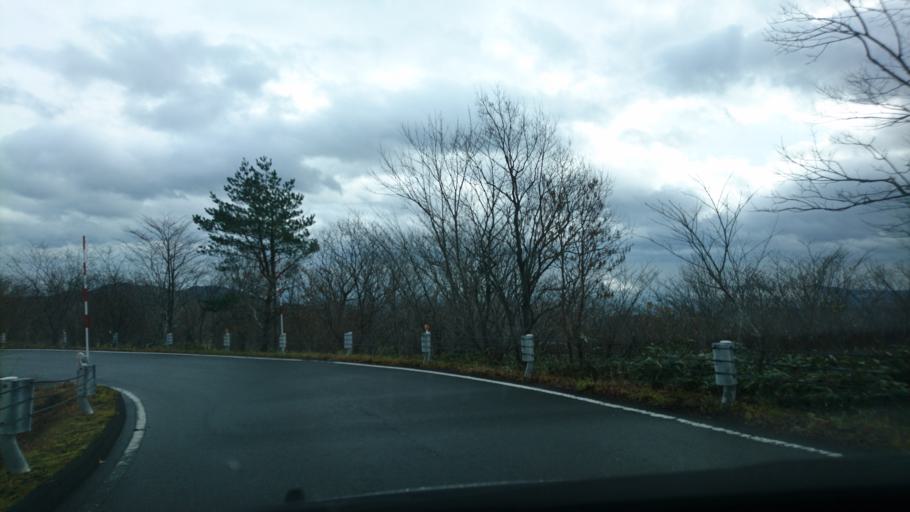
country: JP
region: Iwate
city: Ichinoseki
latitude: 38.9387
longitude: 140.8278
